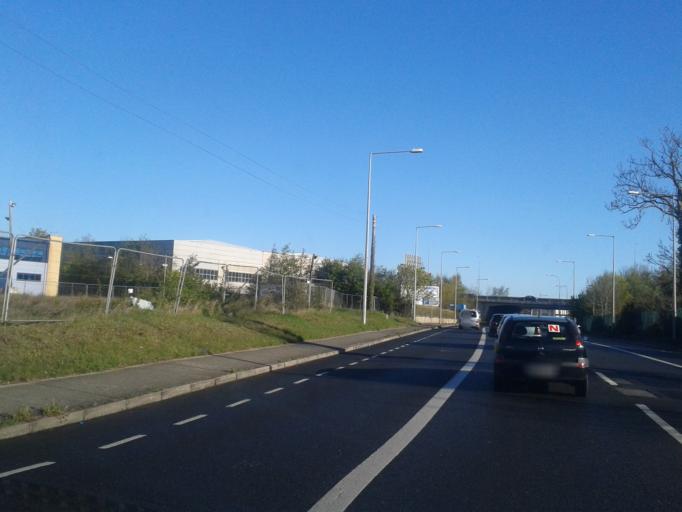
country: IE
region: Leinster
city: Beaumont
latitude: 53.4085
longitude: -6.2379
